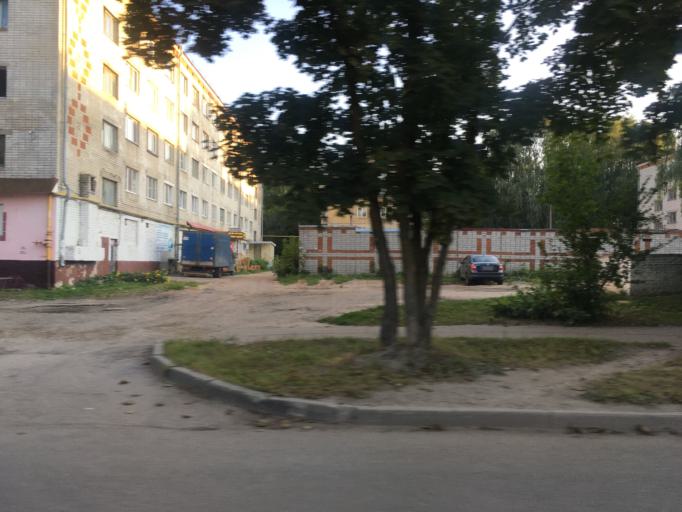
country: RU
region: Mariy-El
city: Yoshkar-Ola
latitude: 56.6487
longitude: 47.8768
